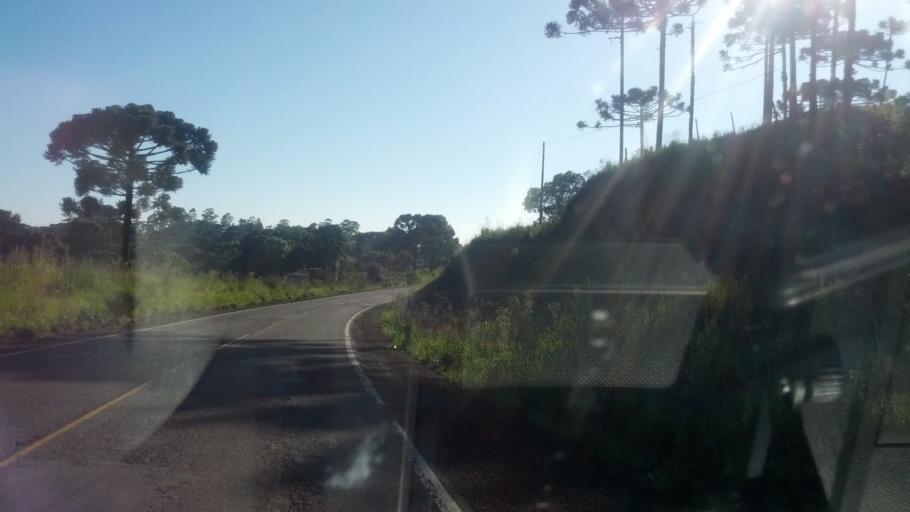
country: BR
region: Santa Catarina
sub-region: Lages
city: Lages
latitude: -27.9135
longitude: -50.5831
